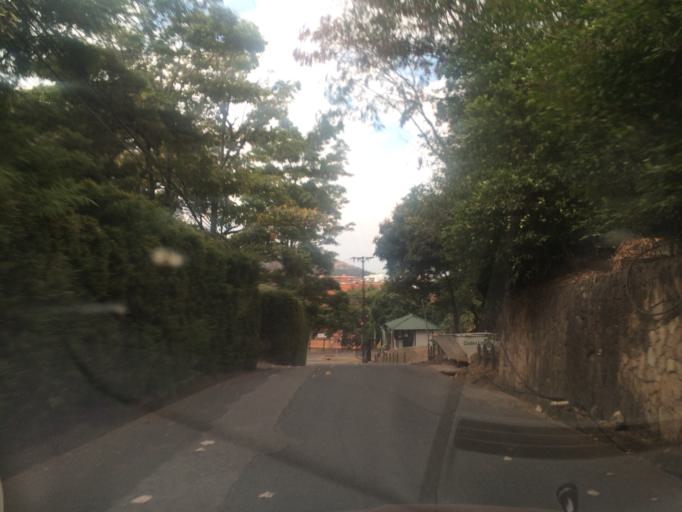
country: CO
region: Valle del Cauca
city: Cali
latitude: 3.4421
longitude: -76.5555
